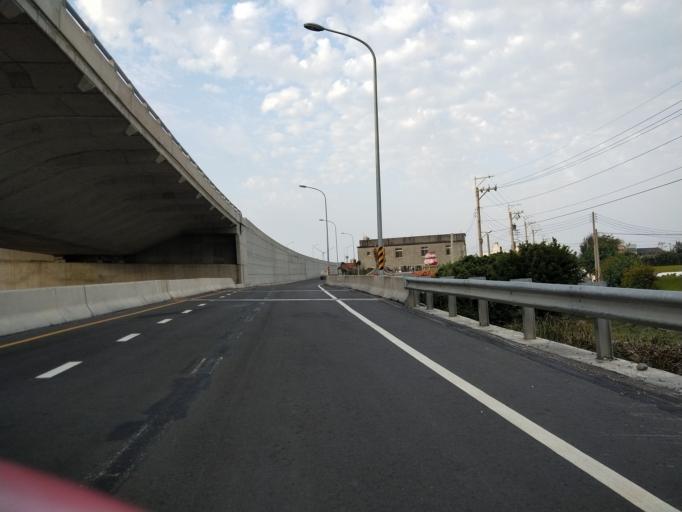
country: TW
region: Taiwan
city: Fengyuan
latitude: 24.3858
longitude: 120.5940
